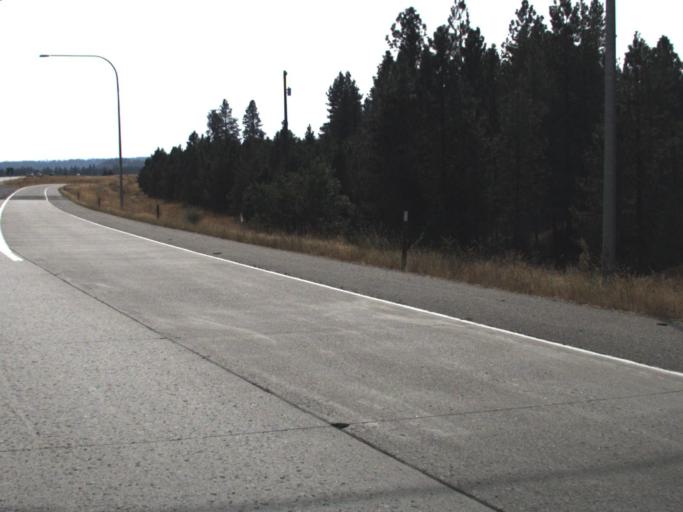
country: US
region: Washington
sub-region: Spokane County
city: Fairwood
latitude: 47.8098
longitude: -117.4065
